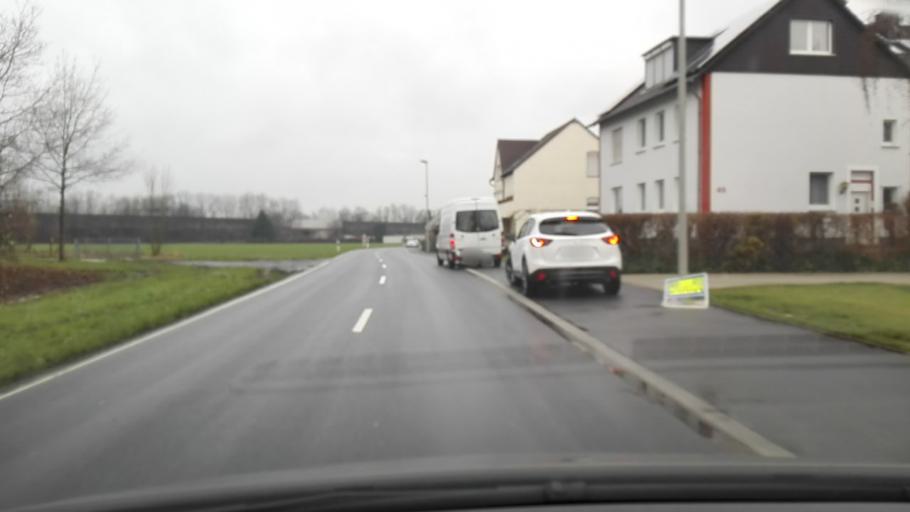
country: DE
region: North Rhine-Westphalia
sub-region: Regierungsbezirk Arnsberg
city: Unna
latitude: 51.5463
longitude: 7.6679
